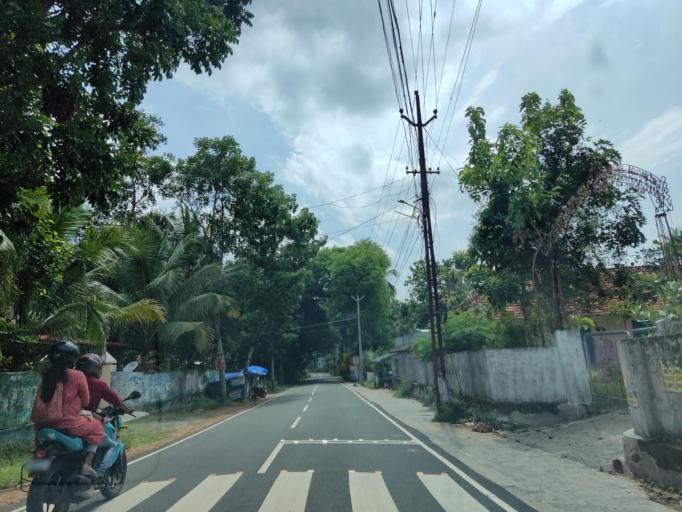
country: IN
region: Kerala
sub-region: Alappuzha
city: Mavelikara
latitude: 9.2677
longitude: 76.5639
